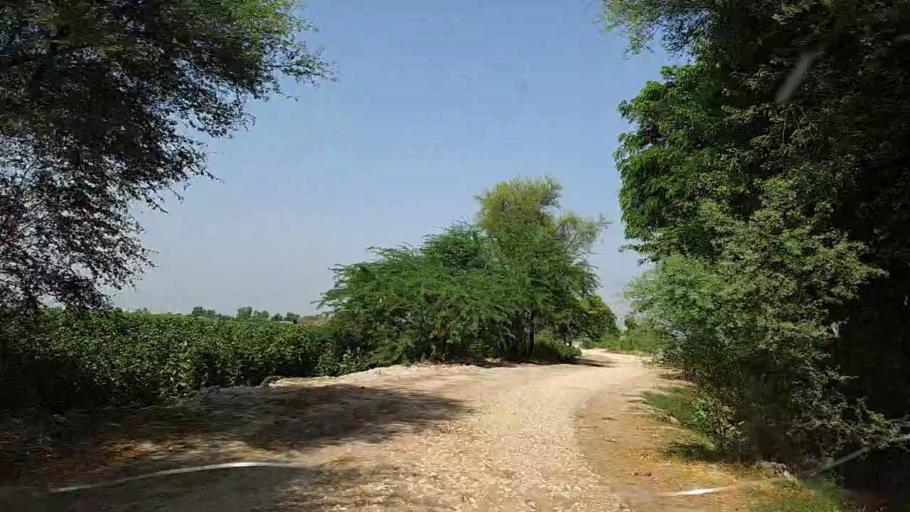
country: PK
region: Sindh
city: Khanpur
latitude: 27.7494
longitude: 69.3527
